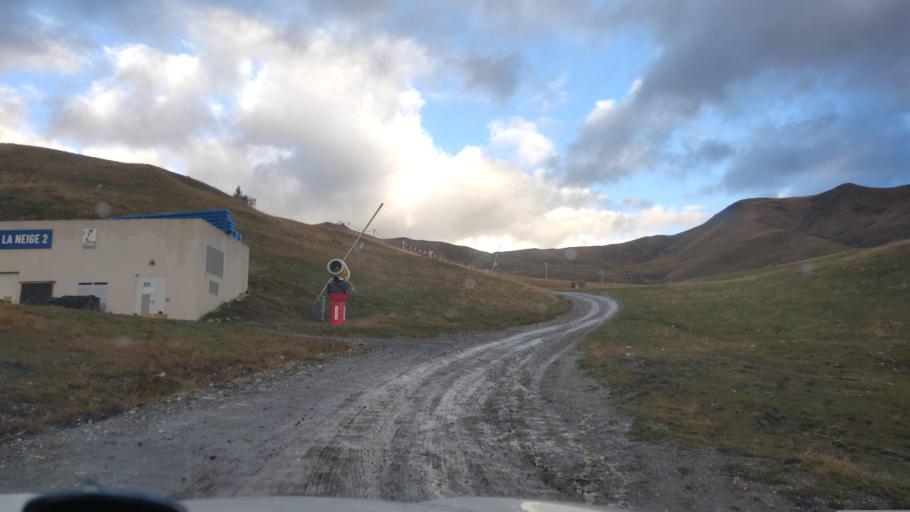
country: FR
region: Rhone-Alpes
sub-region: Departement de la Savoie
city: Saint-Etienne-de-Cuines
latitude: 45.2566
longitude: 6.2519
